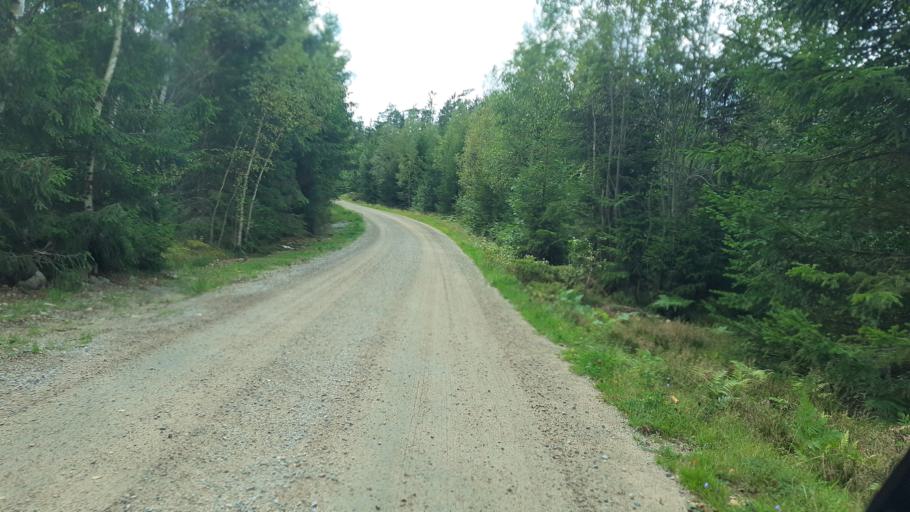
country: SE
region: Blekinge
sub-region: Ronneby Kommun
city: Brakne-Hoby
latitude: 56.4206
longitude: 15.1853
